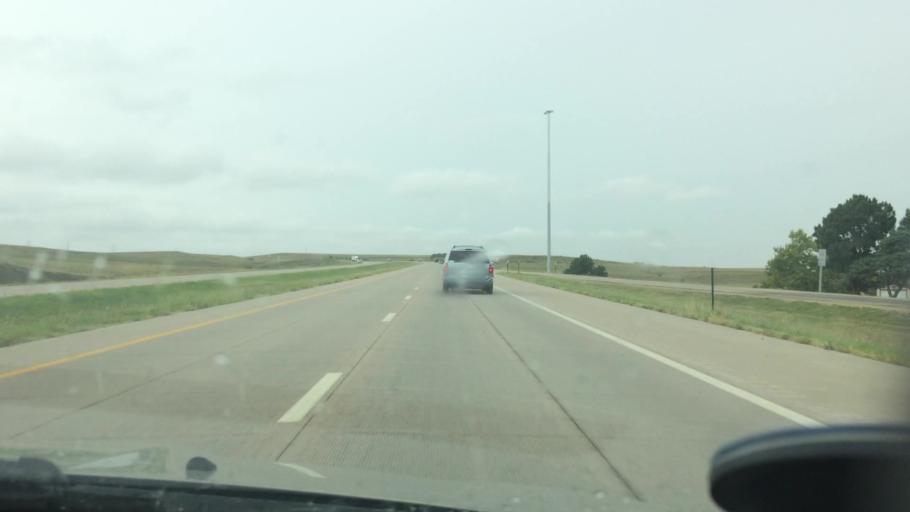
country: US
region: Kansas
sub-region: Ellsworth County
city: Ellsworth
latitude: 38.8566
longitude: -98.1340
